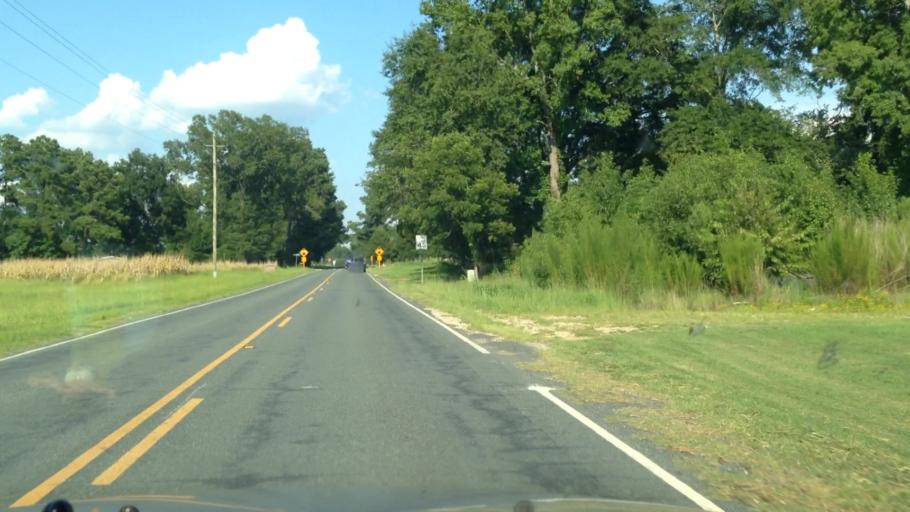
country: US
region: North Carolina
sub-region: Harnett County
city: Buies Creek
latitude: 35.4131
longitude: -78.7178
